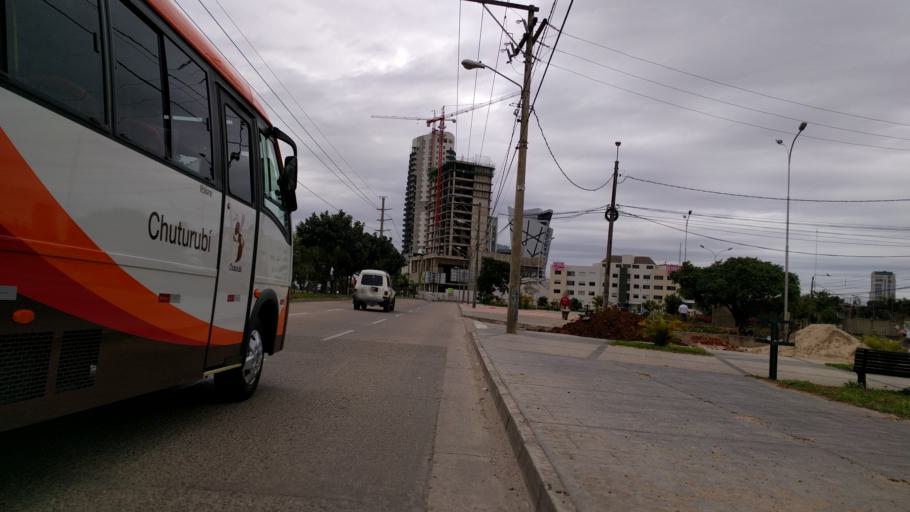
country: BO
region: Santa Cruz
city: Santa Cruz de la Sierra
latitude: -17.7635
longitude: -63.2037
